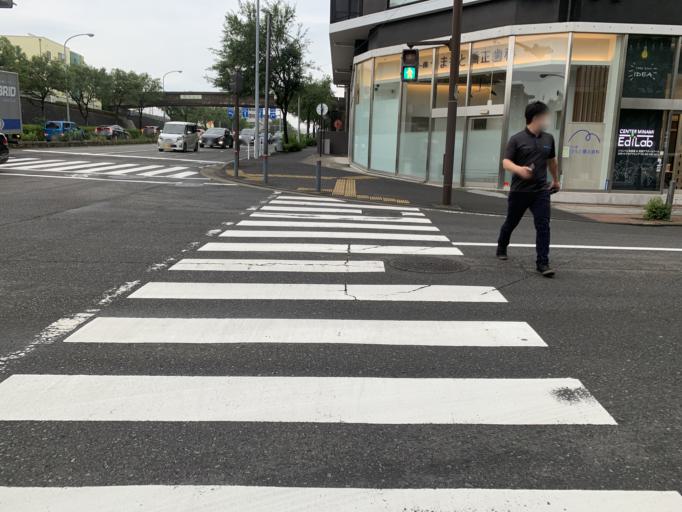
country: JP
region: Kanagawa
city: Yokohama
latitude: 35.5429
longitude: 139.5756
